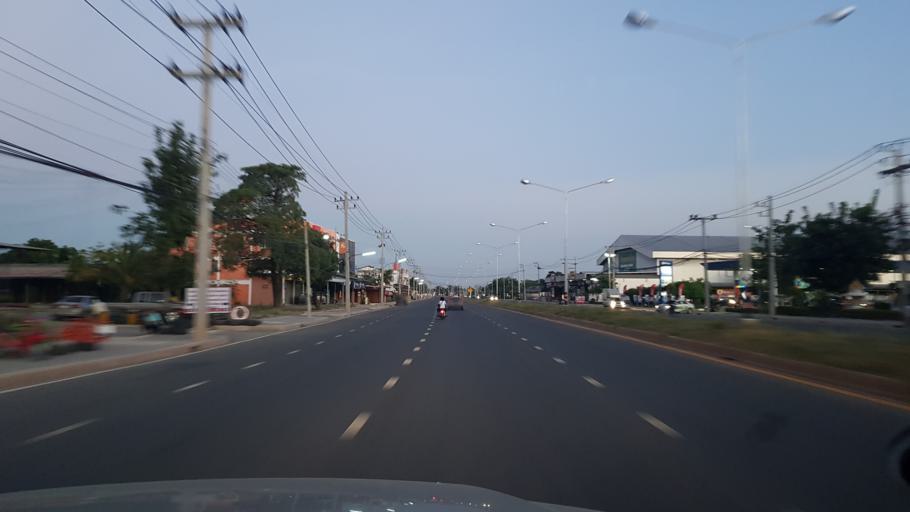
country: TH
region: Chaiyaphum
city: Phu Khiao
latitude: 16.3636
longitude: 102.1420
